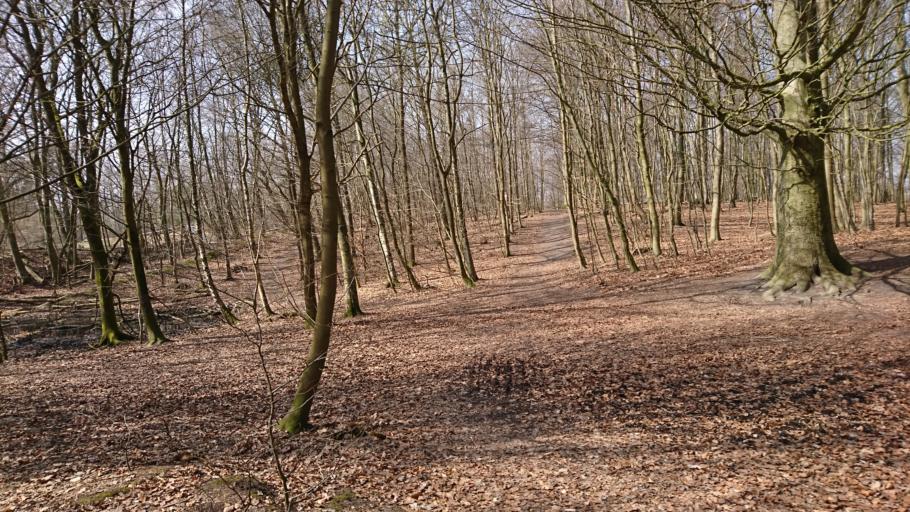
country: DK
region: Capital Region
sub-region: Ballerup Kommune
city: Ballerup
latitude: 55.7542
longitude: 12.3791
